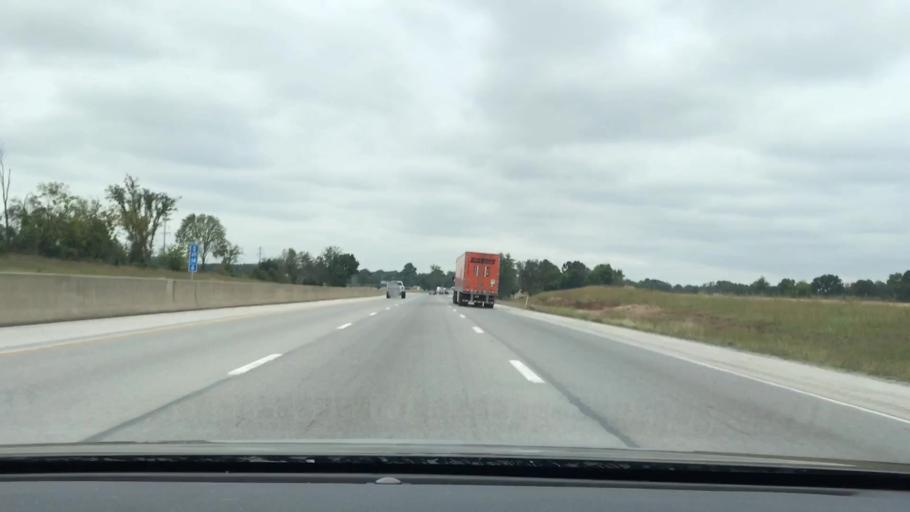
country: US
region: Kentucky
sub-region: Warren County
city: Plano
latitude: 36.8292
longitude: -86.4678
